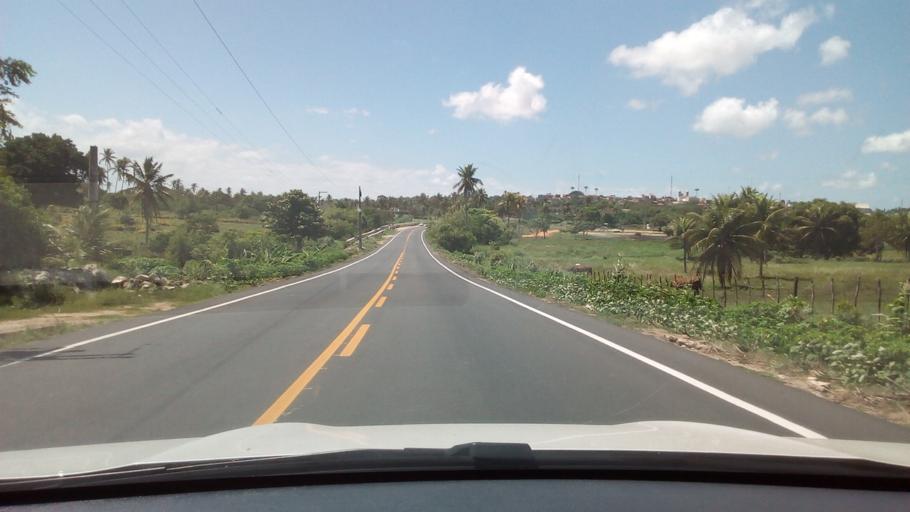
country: BR
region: Rio Grande do Norte
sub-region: Sao Jose De Mipibu
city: Sao Jose de Mipibu
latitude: -6.0829
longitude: -35.2284
